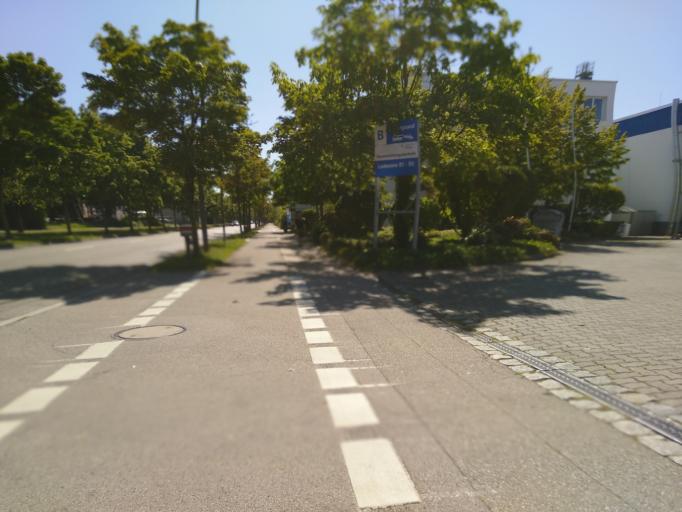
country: DE
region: Bavaria
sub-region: Upper Bavaria
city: Unterfoehring
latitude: 48.1974
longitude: 11.6042
